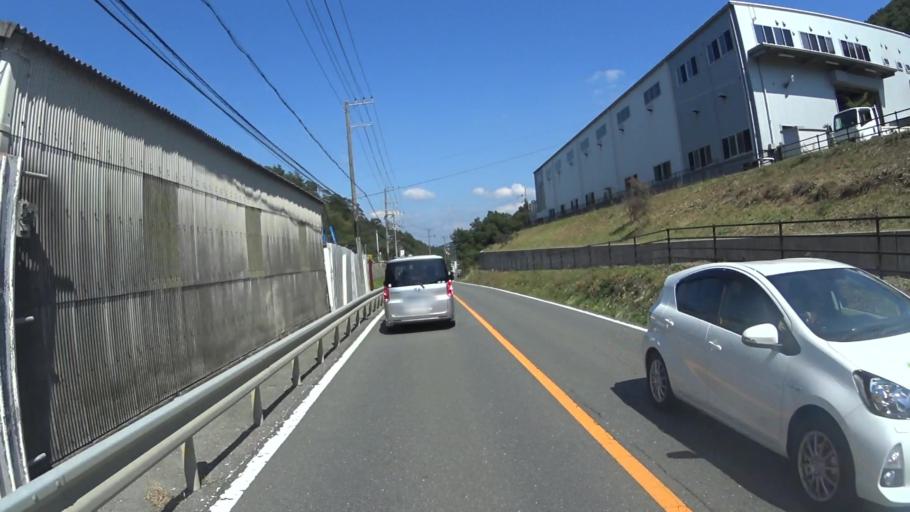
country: JP
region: Kyoto
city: Kameoka
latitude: 34.9509
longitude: 135.4989
